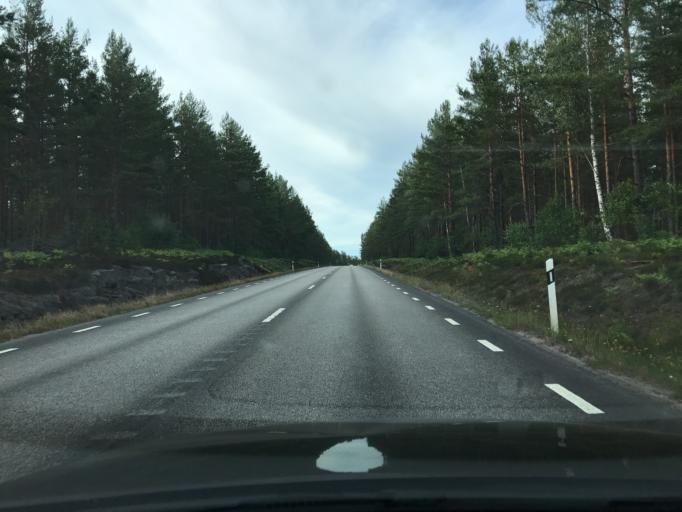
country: SE
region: Kalmar
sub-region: Hultsfreds Kommun
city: Malilla
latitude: 57.4244
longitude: 15.8256
